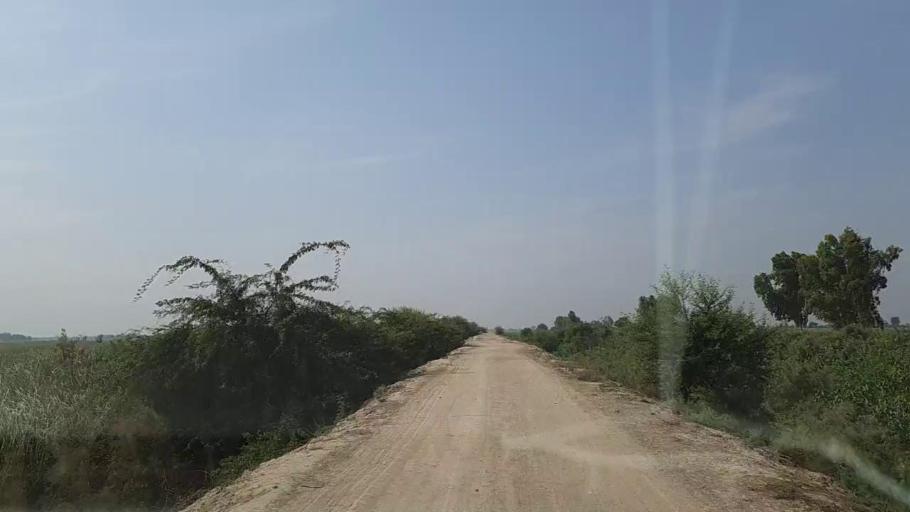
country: PK
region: Sindh
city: Mirpur Batoro
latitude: 24.6516
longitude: 68.2375
